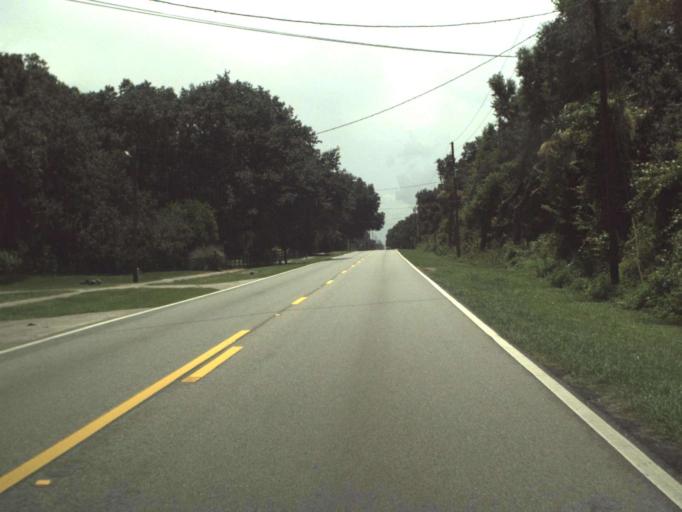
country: US
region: Florida
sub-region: Sumter County
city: Lake Panasoffkee
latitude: 28.7998
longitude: -82.0572
